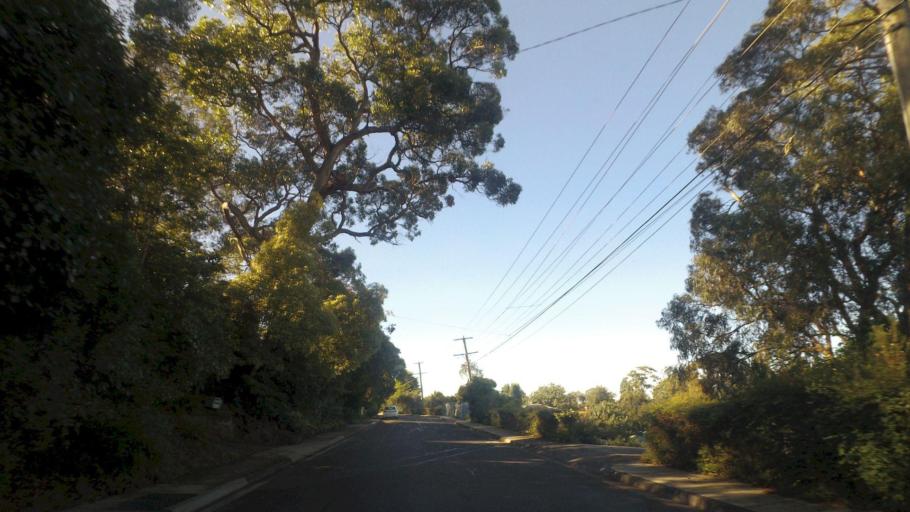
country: AU
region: Victoria
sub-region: Knox
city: Ferntree Gully
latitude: -37.8835
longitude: 145.2899
